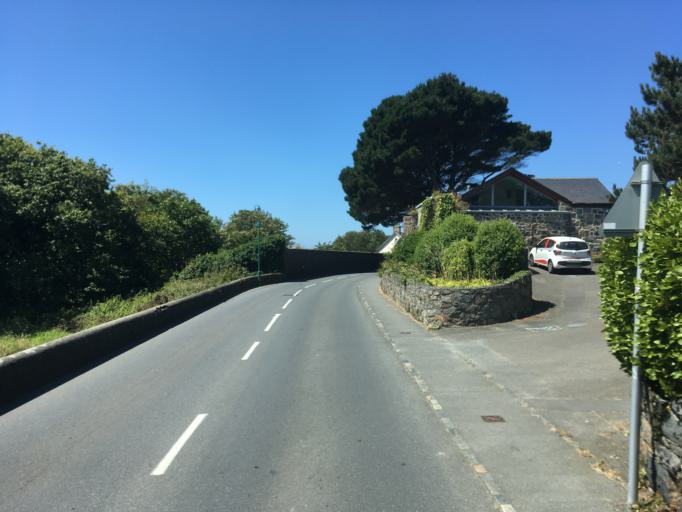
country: GG
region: St Peter Port
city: Saint Peter Port
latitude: 49.4926
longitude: -2.5385
